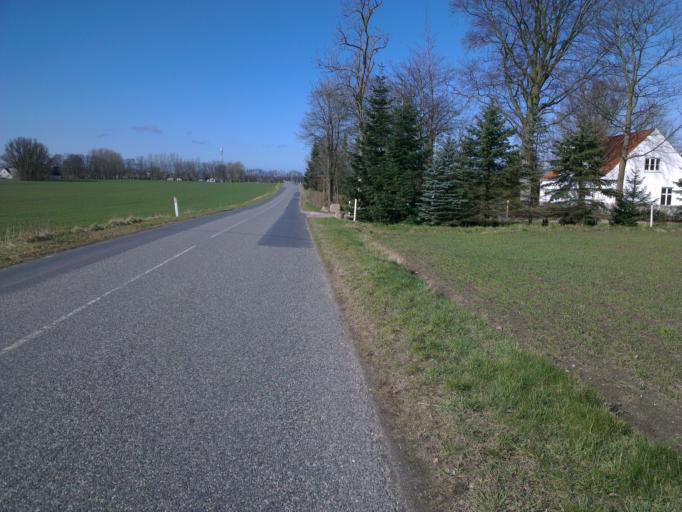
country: DK
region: Capital Region
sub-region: Hillerod Kommune
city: Skaevinge
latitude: 55.8830
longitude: 12.1191
